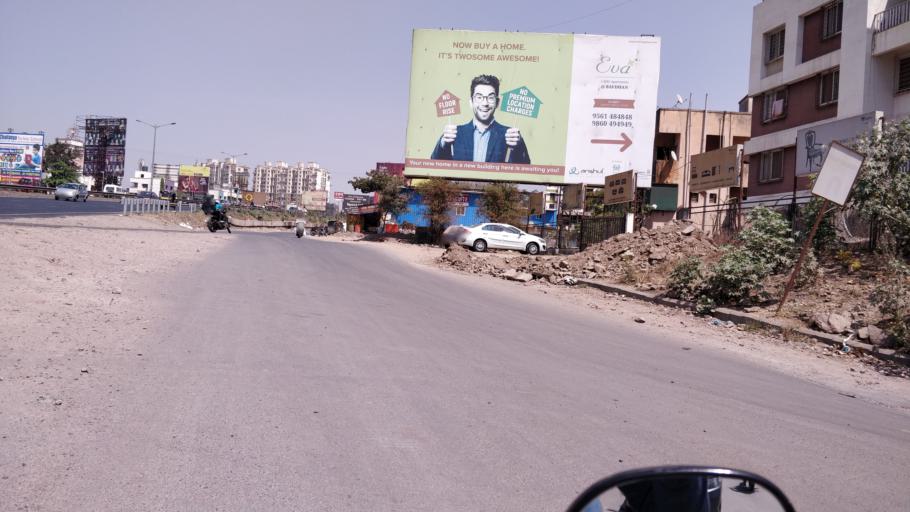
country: IN
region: Maharashtra
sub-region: Pune Division
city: Kharakvasla
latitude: 18.5136
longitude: 73.7700
